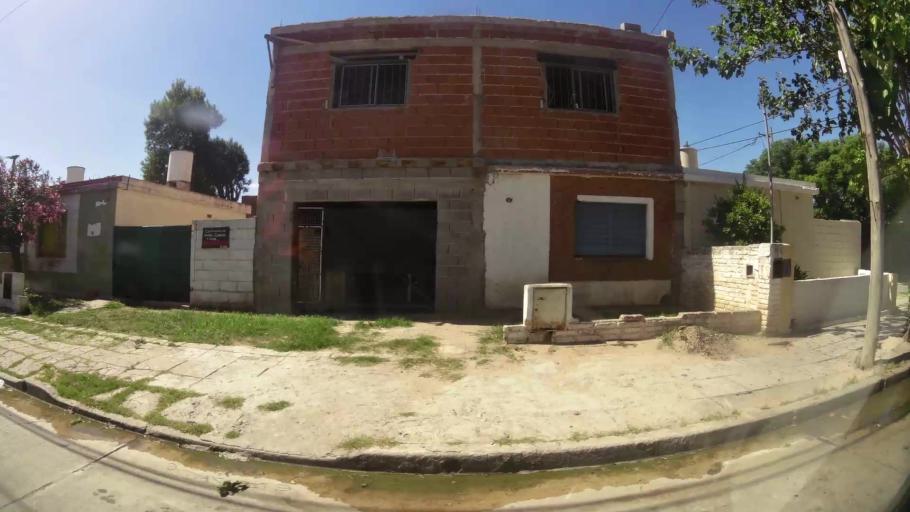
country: AR
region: Cordoba
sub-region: Departamento de Capital
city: Cordoba
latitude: -31.3657
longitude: -64.1390
